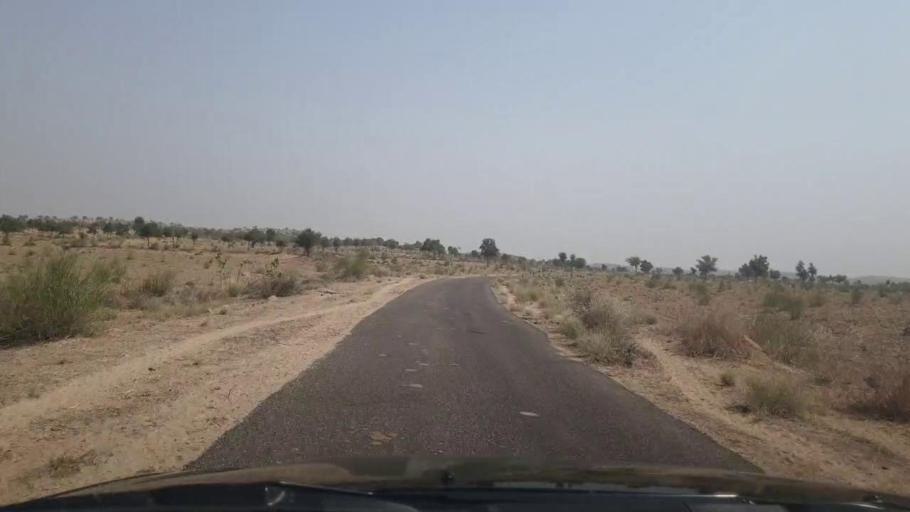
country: PK
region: Sindh
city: Islamkot
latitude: 24.9437
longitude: 70.3831
